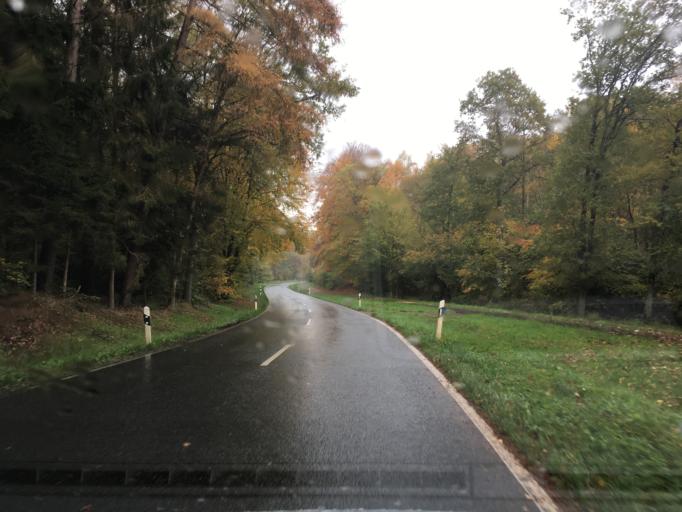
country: DE
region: North Rhine-Westphalia
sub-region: Regierungsbezirk Munster
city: Klein Reken
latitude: 51.8430
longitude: 7.0305
